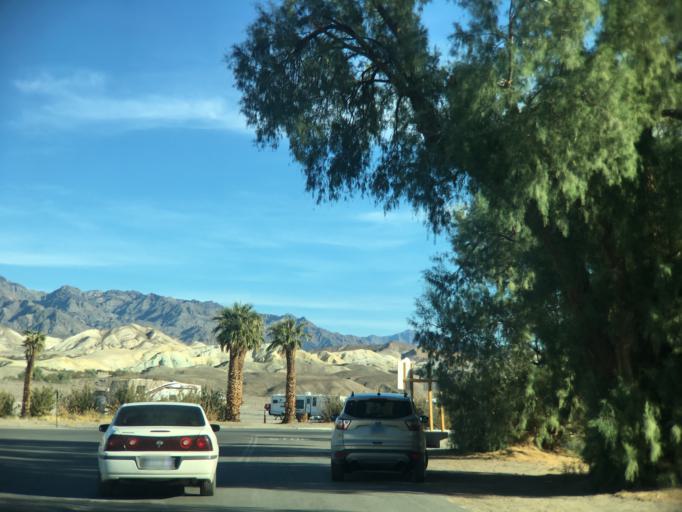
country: US
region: Nevada
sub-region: Nye County
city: Beatty
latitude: 36.4598
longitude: -116.8663
